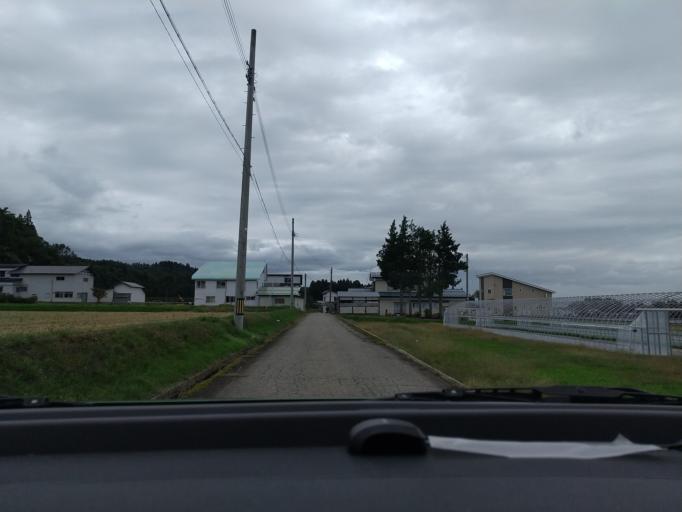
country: JP
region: Akita
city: Yokotemachi
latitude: 39.3445
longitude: 140.5766
